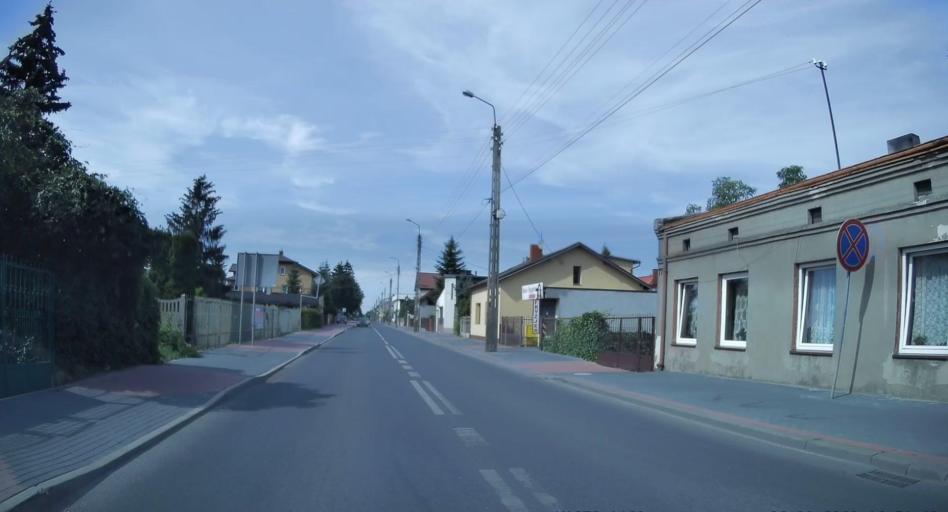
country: PL
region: Lodz Voivodeship
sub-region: Powiat tomaszowski
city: Tomaszow Mazowiecki
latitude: 51.5256
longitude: 19.9976
